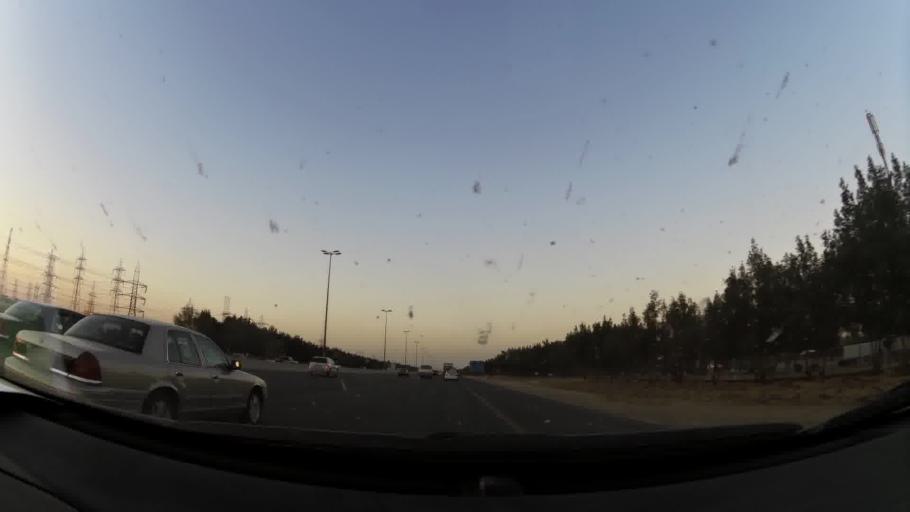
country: KW
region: Mubarak al Kabir
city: Mubarak al Kabir
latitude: 29.1845
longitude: 48.0662
